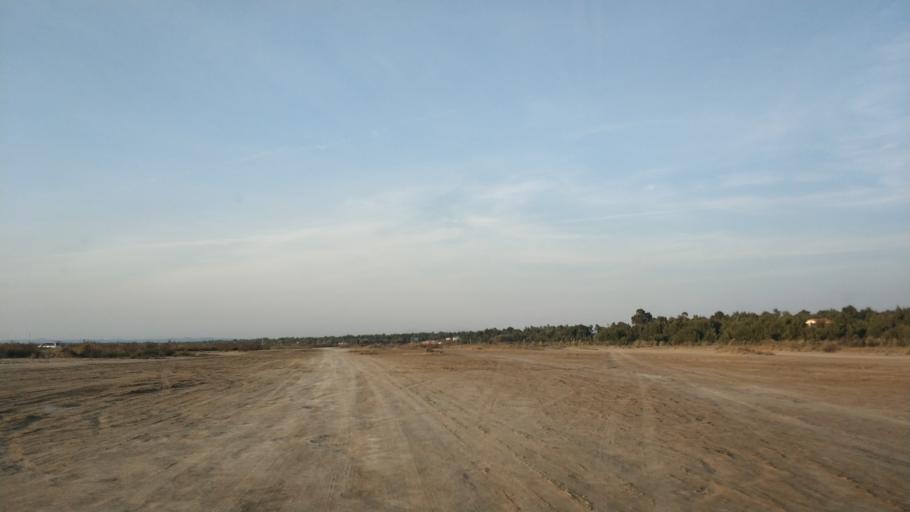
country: AL
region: Fier
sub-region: Rrethi i Lushnjes
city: Divjake
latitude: 40.9615
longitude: 19.4729
